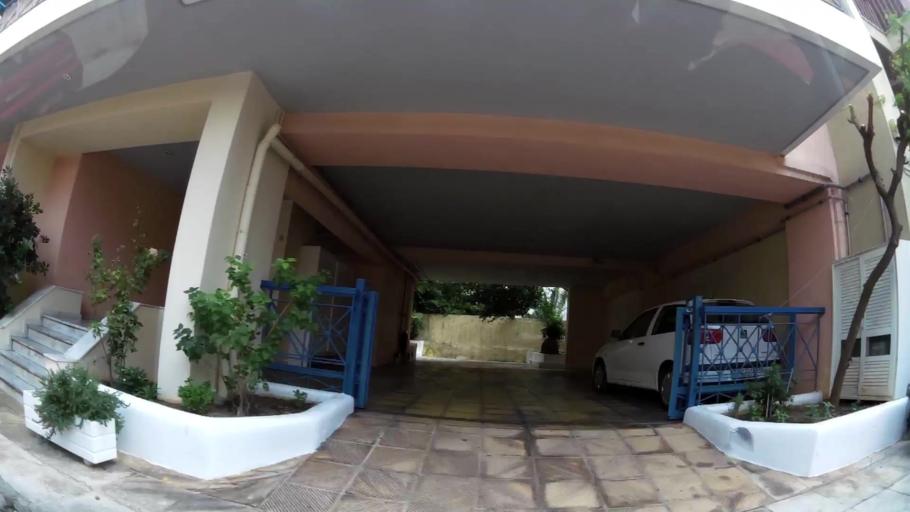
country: GR
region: Attica
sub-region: Nomarchia Athinas
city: Athens
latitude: 37.9721
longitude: 23.7130
